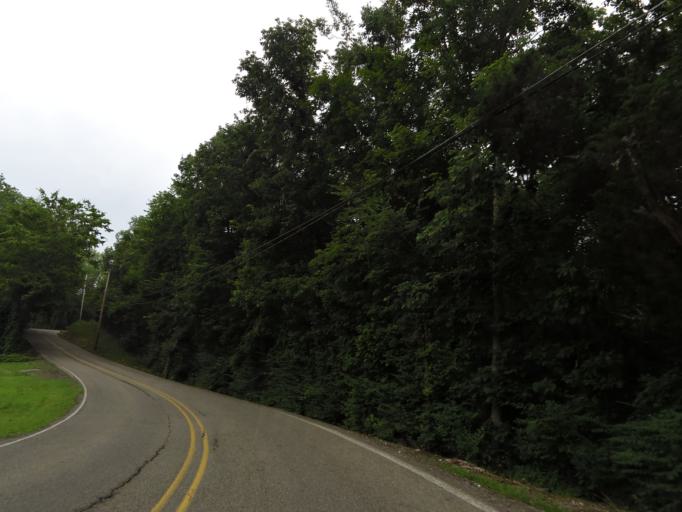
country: US
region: Tennessee
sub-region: Knox County
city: Knoxville
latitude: 35.9405
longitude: -83.8751
